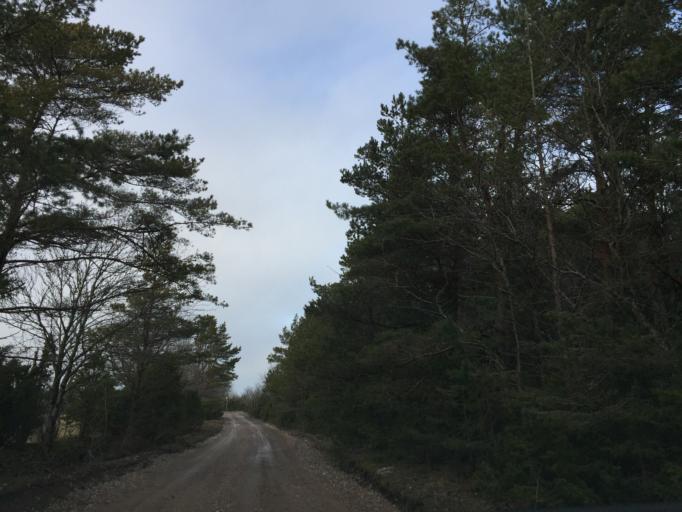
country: EE
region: Saare
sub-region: Kuressaare linn
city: Kuressaare
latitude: 58.4929
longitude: 21.9329
